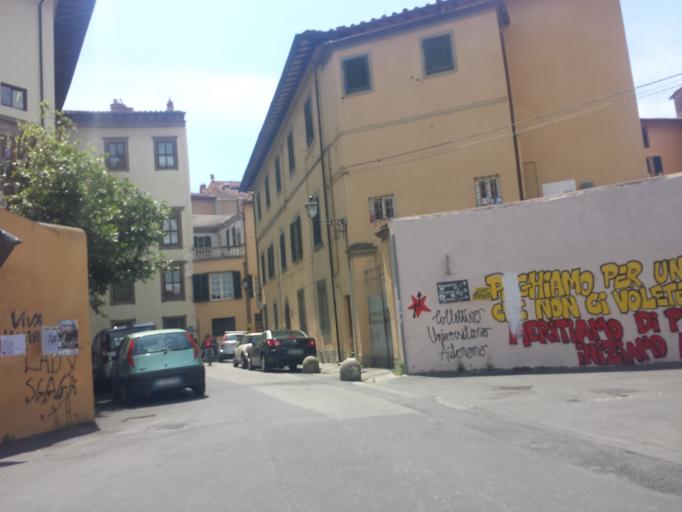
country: IT
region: Tuscany
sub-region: Province of Pisa
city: Pisa
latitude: 43.7204
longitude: 10.3999
